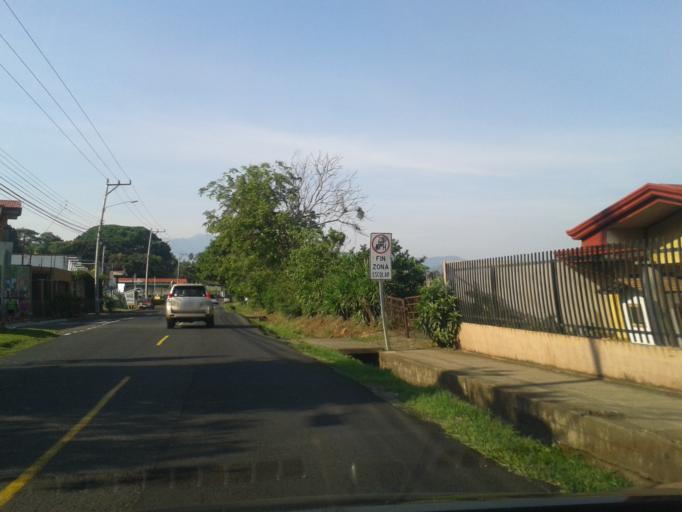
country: CR
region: Heredia
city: Llorente
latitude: 10.0095
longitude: -84.1521
